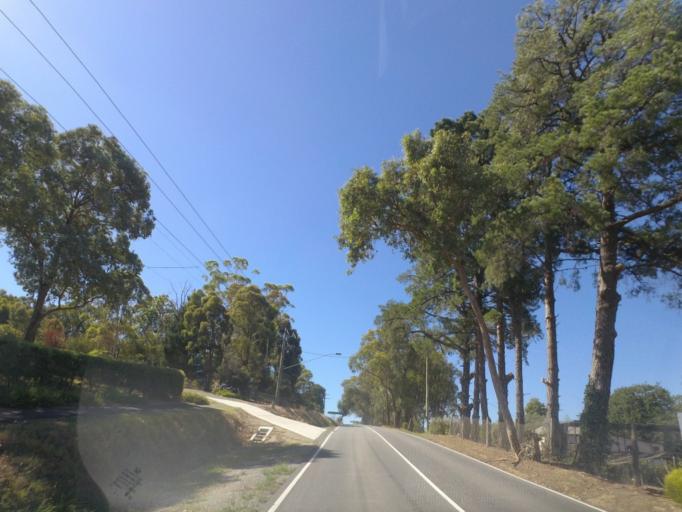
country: AU
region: Victoria
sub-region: Yarra Ranges
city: Chirnside Park
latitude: -37.7365
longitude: 145.2826
